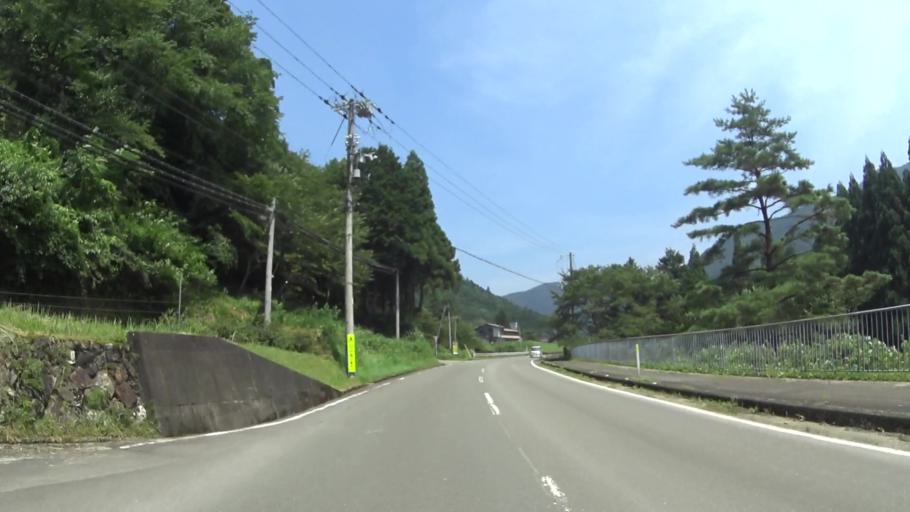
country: JP
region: Kyoto
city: Ayabe
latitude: 35.2681
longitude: 135.4302
